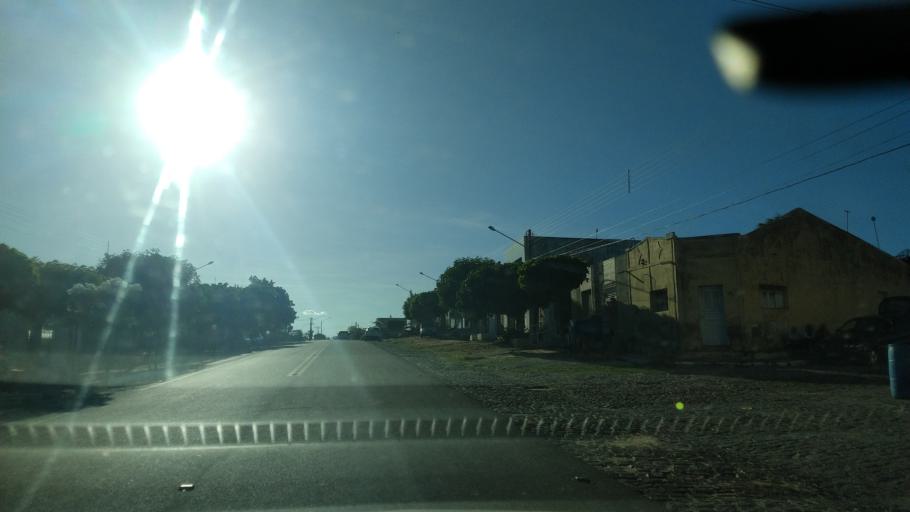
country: BR
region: Rio Grande do Norte
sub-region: Sao Jose Do Campestre
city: Sao Jose do Campestre
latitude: -6.3155
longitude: -35.7115
